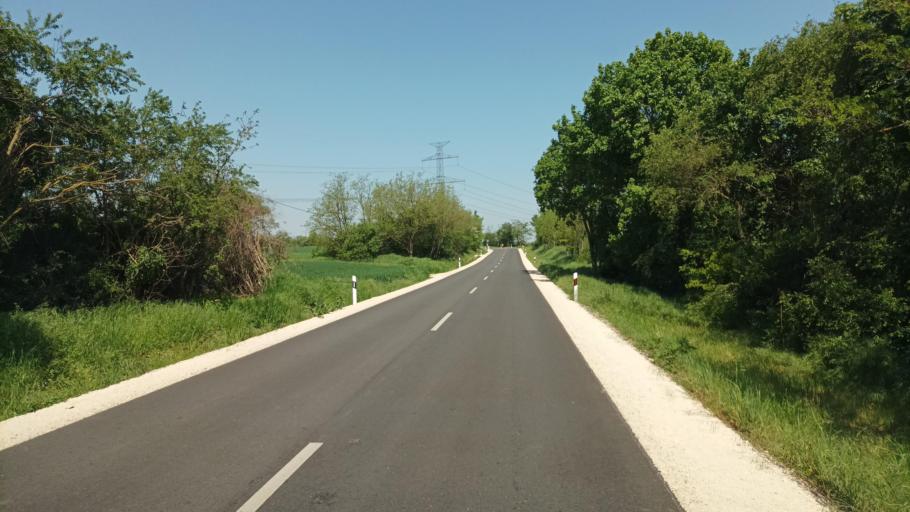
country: HU
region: Pest
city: Gomba
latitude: 47.3831
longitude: 19.5075
